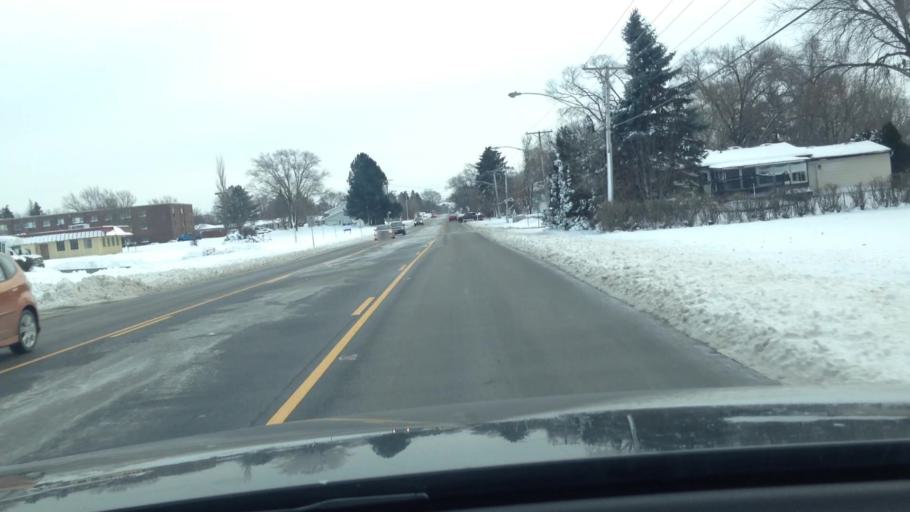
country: US
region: Illinois
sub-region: McHenry County
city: Woodstock
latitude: 42.3387
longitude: -88.4433
